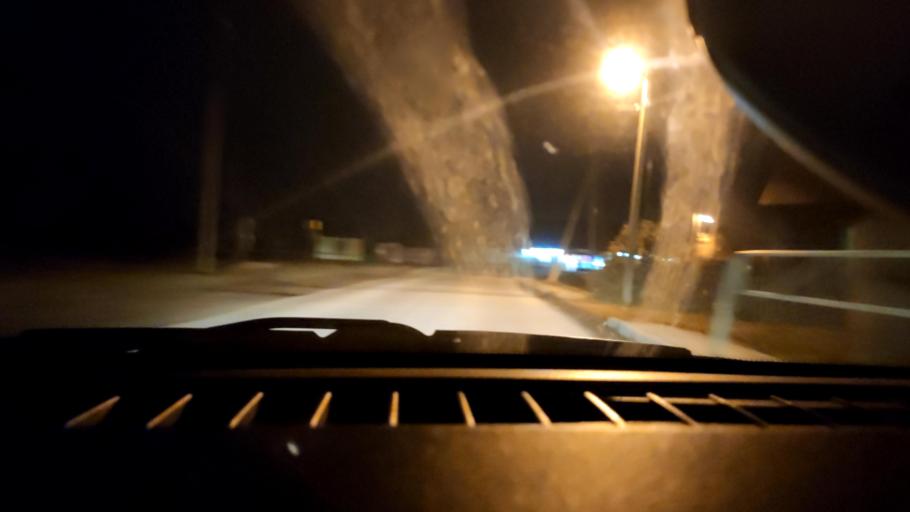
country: RU
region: Perm
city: Ferma
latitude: 57.8960
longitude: 56.3015
